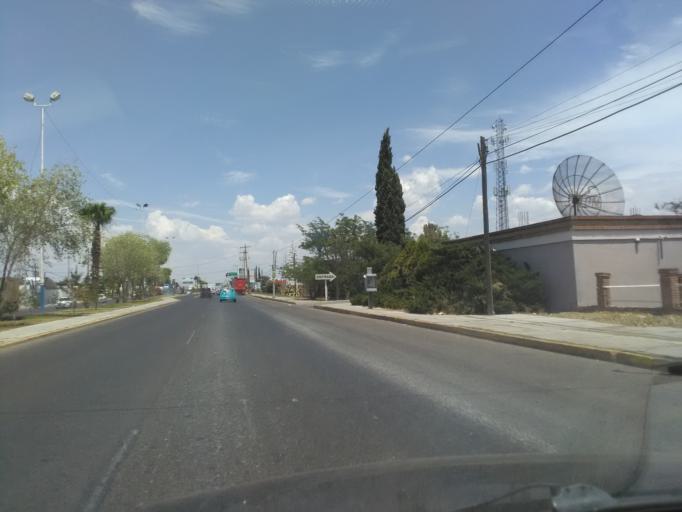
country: MX
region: Durango
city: Victoria de Durango
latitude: 24.0305
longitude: -104.6153
